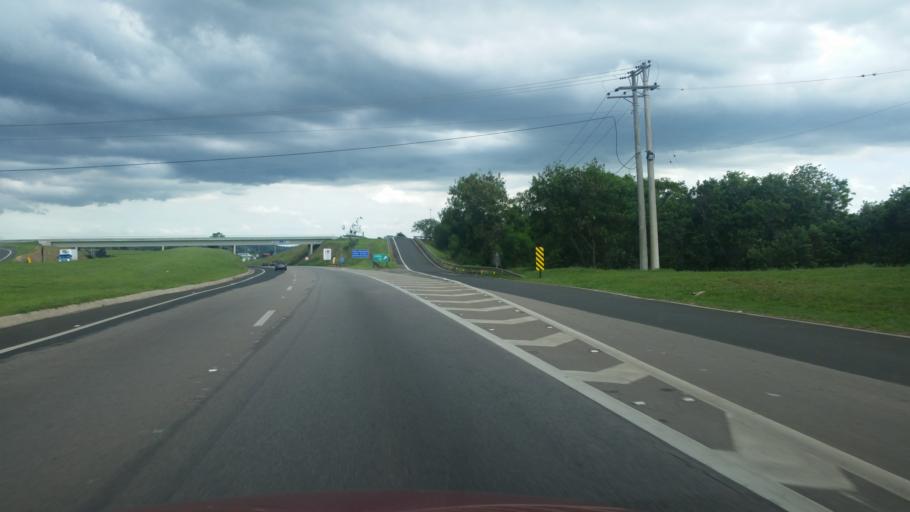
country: BR
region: Sao Paulo
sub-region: Boituva
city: Boituva
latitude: -23.3164
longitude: -47.6399
